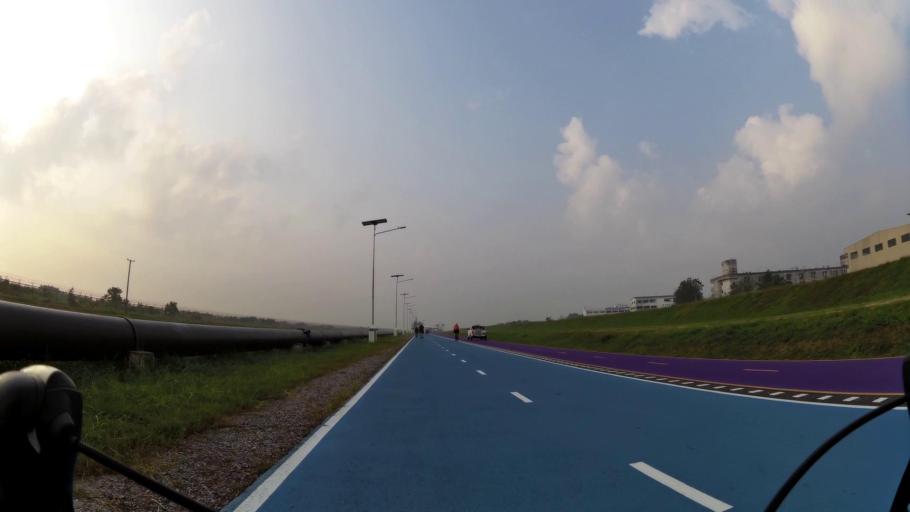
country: TH
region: Bangkok
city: Lat Krabang
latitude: 13.6818
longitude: 100.7654
